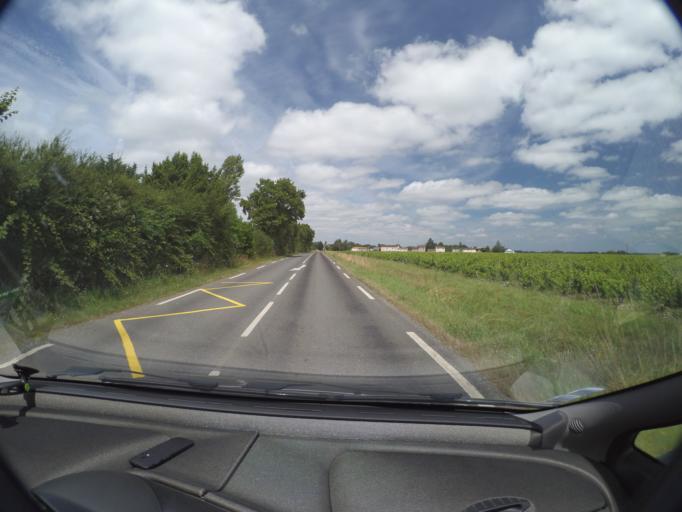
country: FR
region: Pays de la Loire
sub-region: Departement de la Loire-Atlantique
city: Gorges
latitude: 47.1114
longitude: -1.2951
